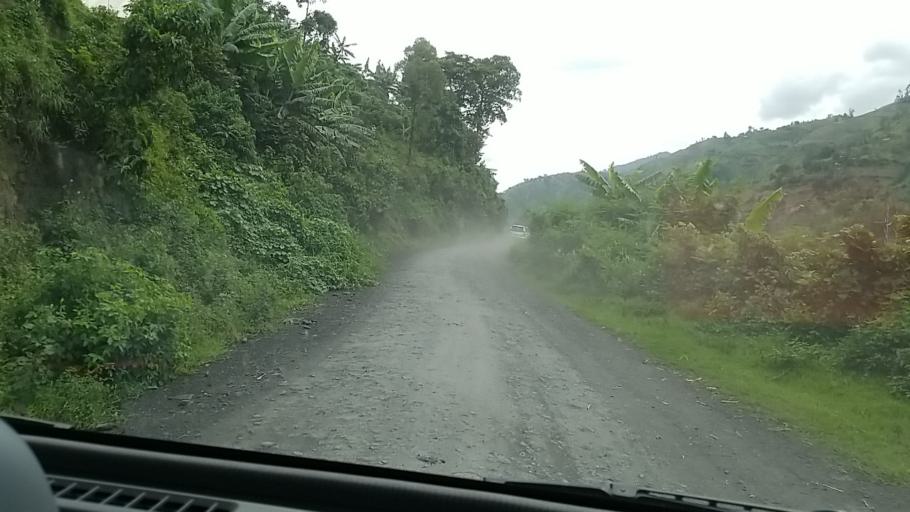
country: CD
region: Nord Kivu
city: Sake
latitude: -1.7443
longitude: 28.9900
